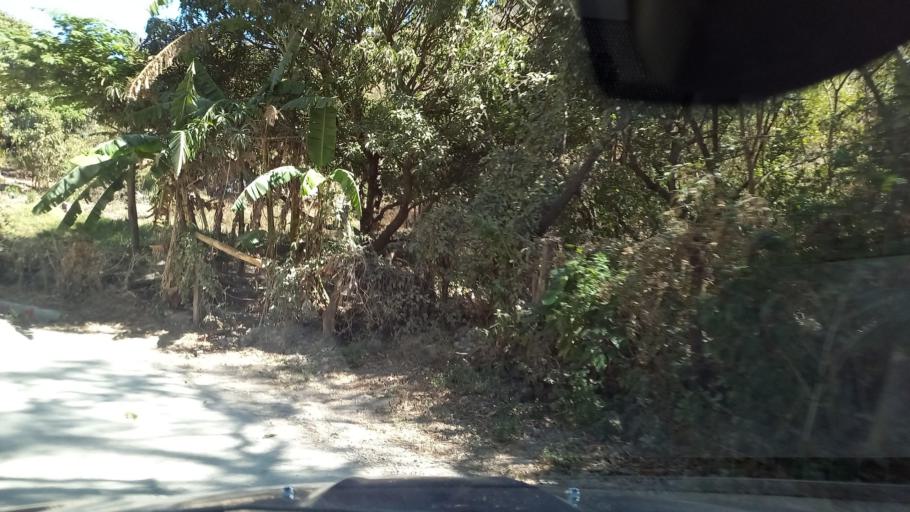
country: SV
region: Santa Ana
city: Metapan
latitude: 14.3714
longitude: -89.4943
